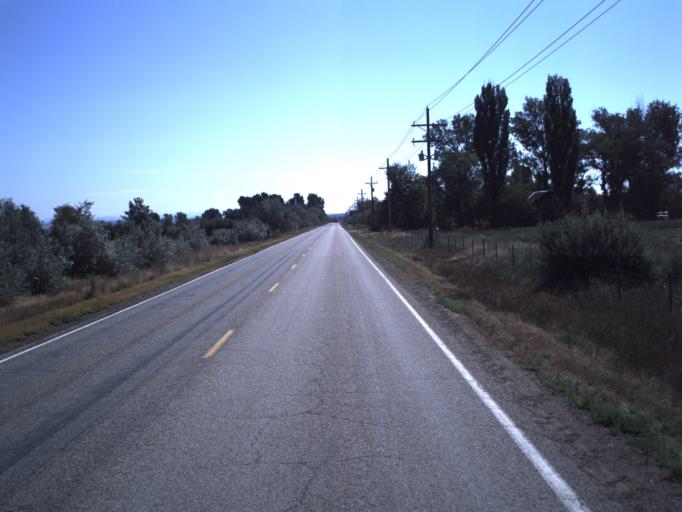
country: US
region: Utah
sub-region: Duchesne County
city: Roosevelt
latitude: 40.2582
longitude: -110.1218
